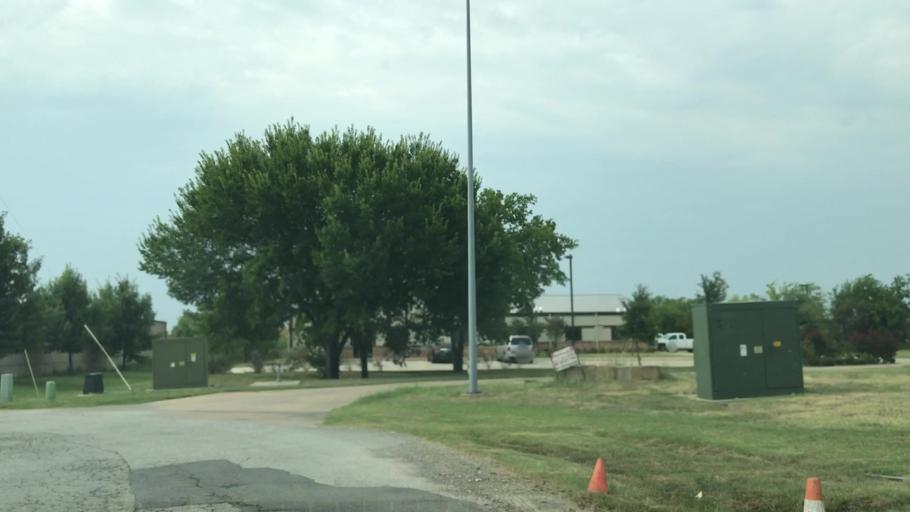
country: US
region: Texas
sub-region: Tarrant County
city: Keller
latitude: 32.9104
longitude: -97.2641
